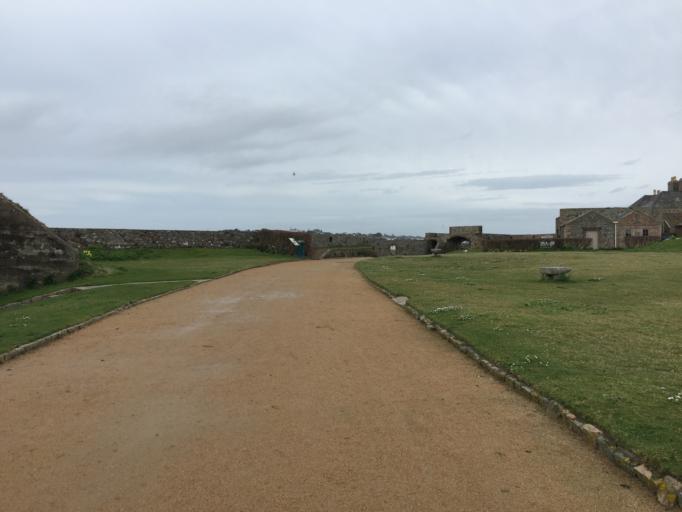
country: JE
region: St Helier
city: Saint Helier
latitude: 49.1773
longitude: -2.1251
